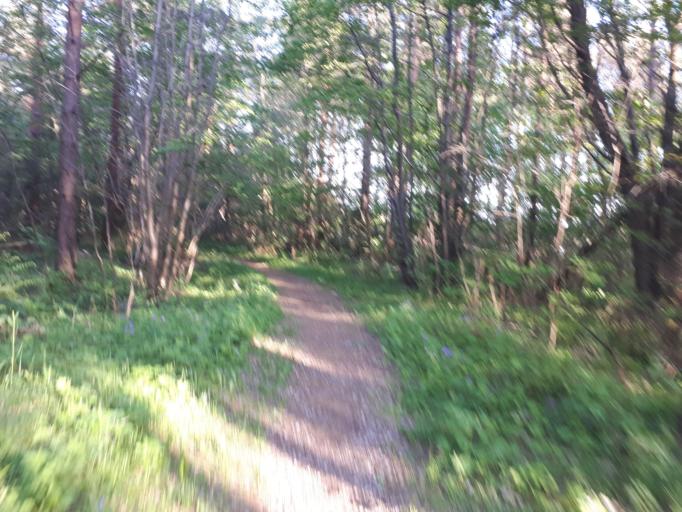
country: SE
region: Gotland
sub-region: Gotland
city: Visby
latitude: 57.6031
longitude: 18.2996
